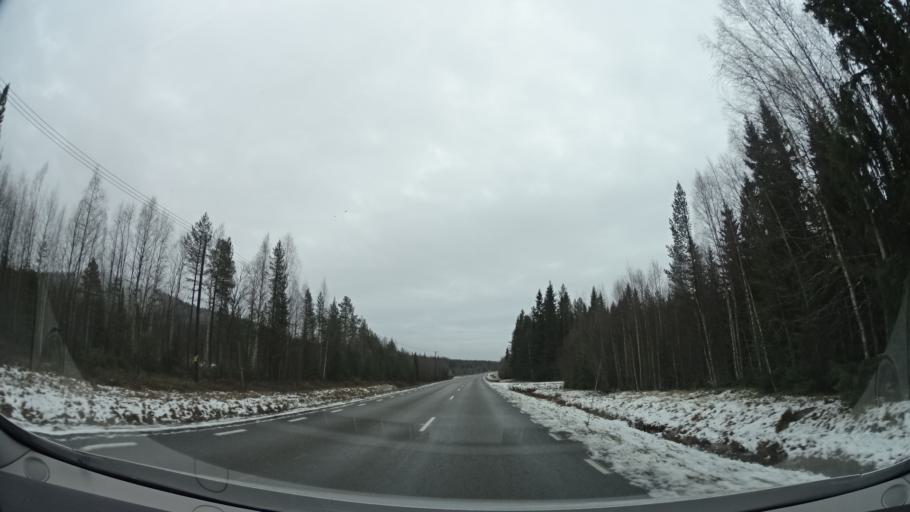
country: SE
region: Jaemtland
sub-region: Stroemsunds Kommun
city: Stroemsund
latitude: 63.9227
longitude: 15.5133
